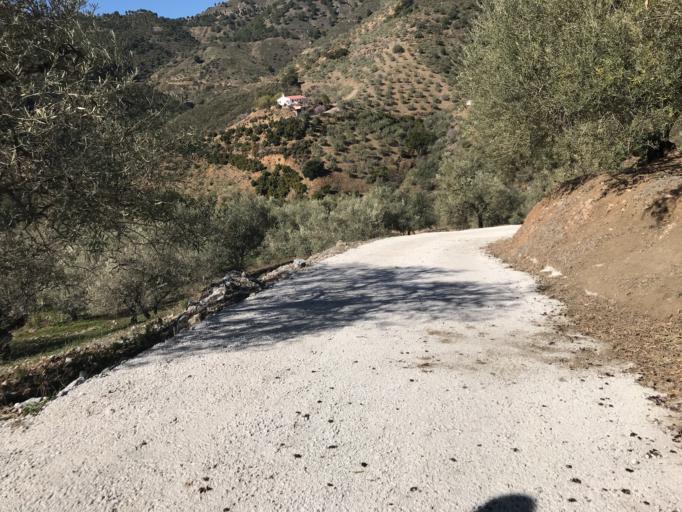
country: ES
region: Andalusia
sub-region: Provincia de Malaga
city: Canillas de Albaida
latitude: 36.8604
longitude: -3.9883
